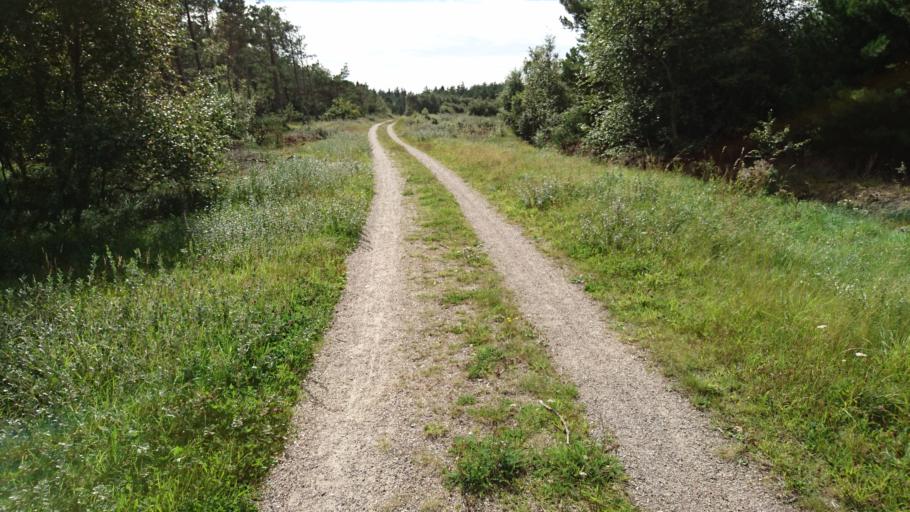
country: DK
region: North Denmark
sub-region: Frederikshavn Kommune
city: Skagen
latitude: 57.7140
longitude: 10.5142
